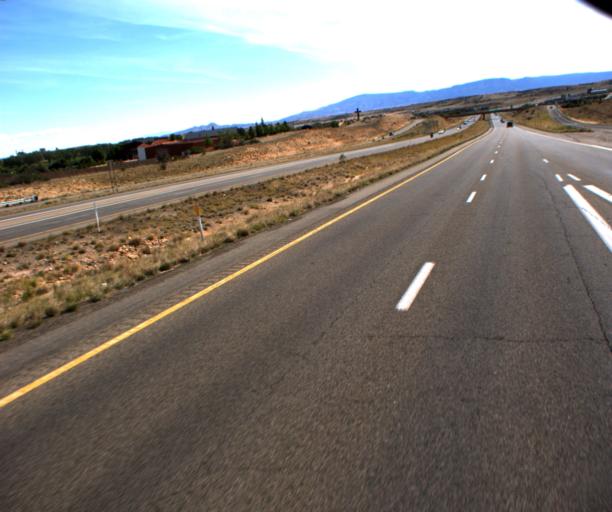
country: US
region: Arizona
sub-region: Yavapai County
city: Prescott
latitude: 34.6334
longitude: -112.4233
